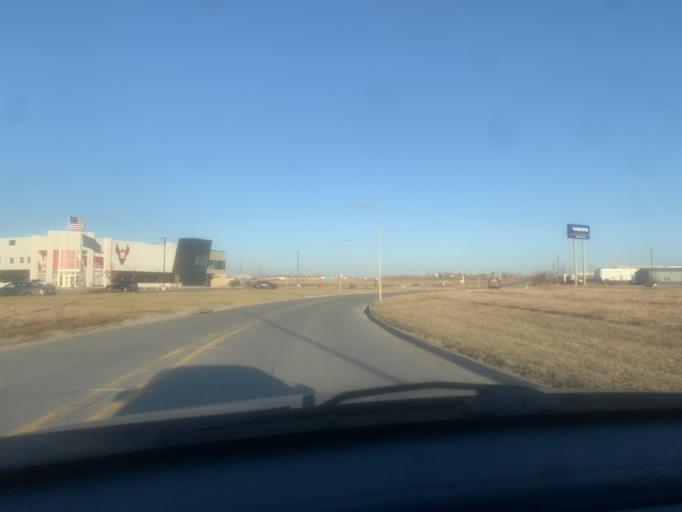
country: US
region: Nebraska
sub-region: Sarpy County
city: Chalco
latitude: 41.1452
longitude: -96.1564
